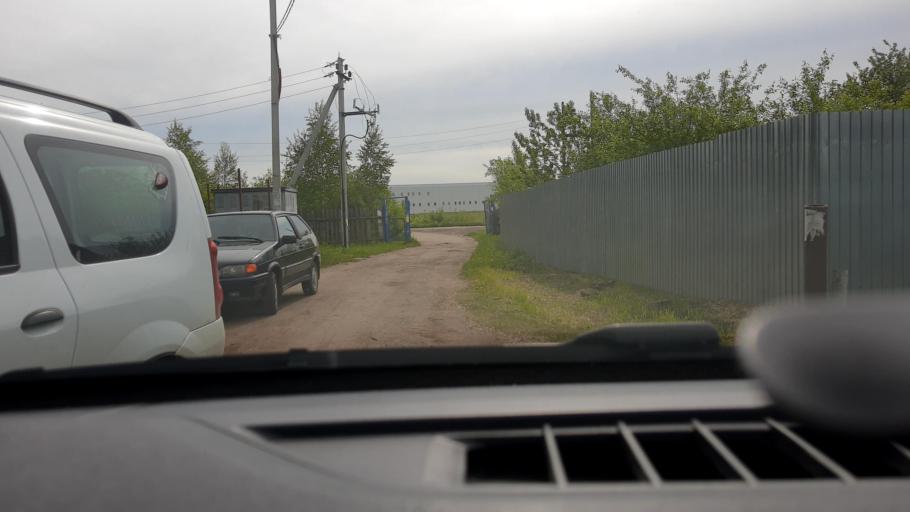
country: RU
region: Nizjnij Novgorod
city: Gorbatovka
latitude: 56.3054
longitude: 43.7686
